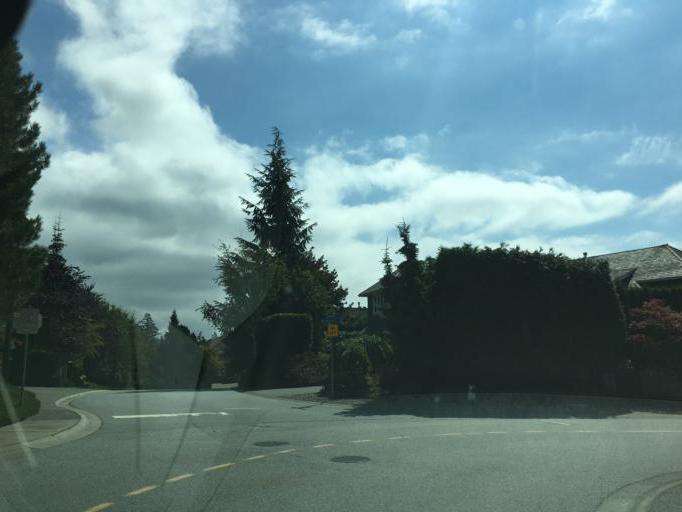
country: CA
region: British Columbia
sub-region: Greater Vancouver Regional District
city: Bowen Island
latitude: 49.3427
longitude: -123.2570
